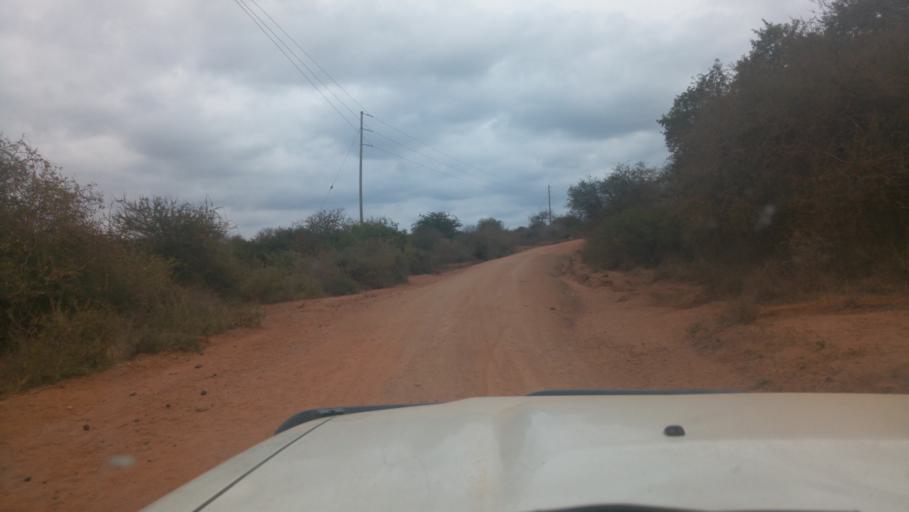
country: KE
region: Makueni
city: Makueni
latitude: -1.9563
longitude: 38.0687
